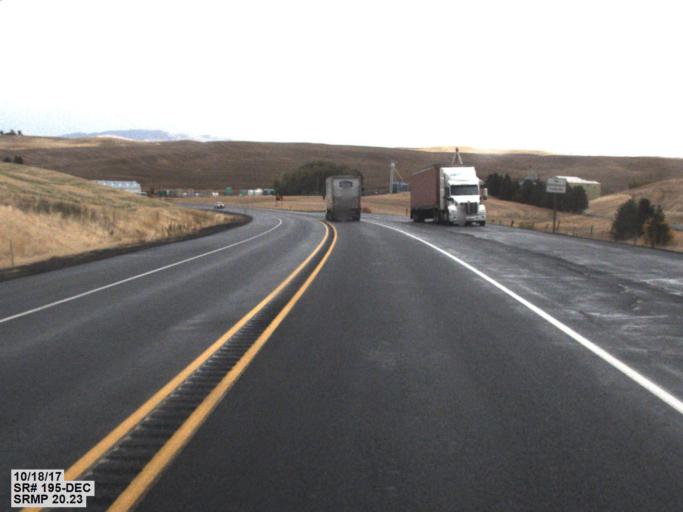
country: US
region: Washington
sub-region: Whitman County
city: Pullman
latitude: 46.7082
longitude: -117.2104
